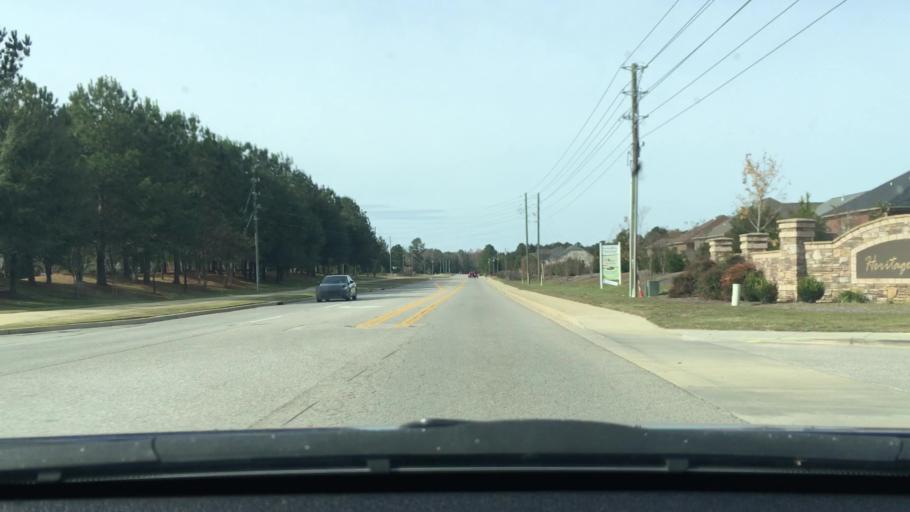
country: US
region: South Carolina
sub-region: Sumter County
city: Cane Savannah
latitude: 33.9303
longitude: -80.4123
